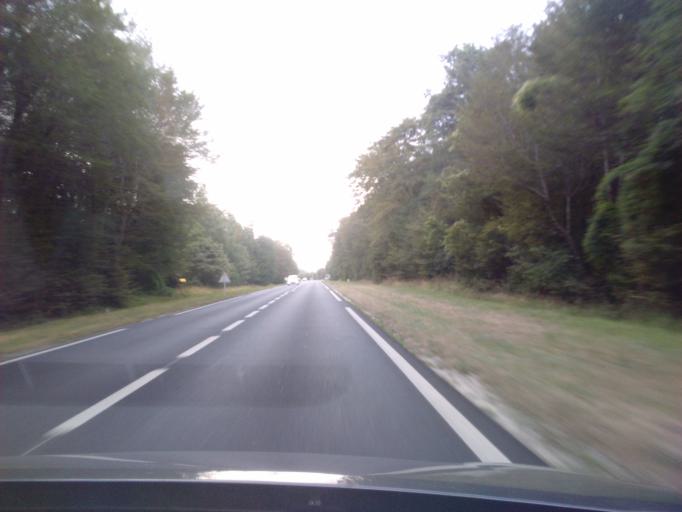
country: FR
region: Centre
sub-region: Departement du Loir-et-Cher
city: Cellettes
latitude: 47.5397
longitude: 1.3751
